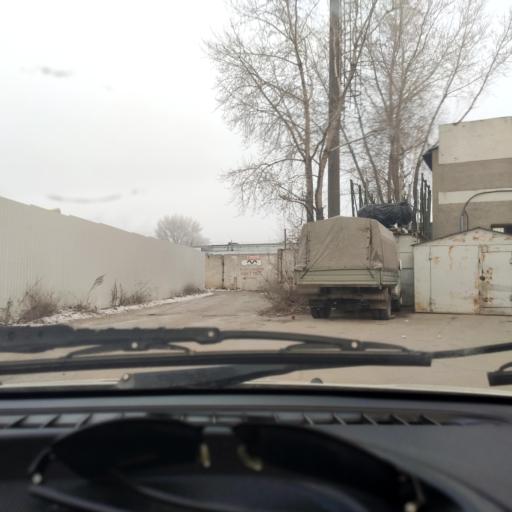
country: RU
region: Samara
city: Zhigulevsk
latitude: 53.4762
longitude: 49.5045
